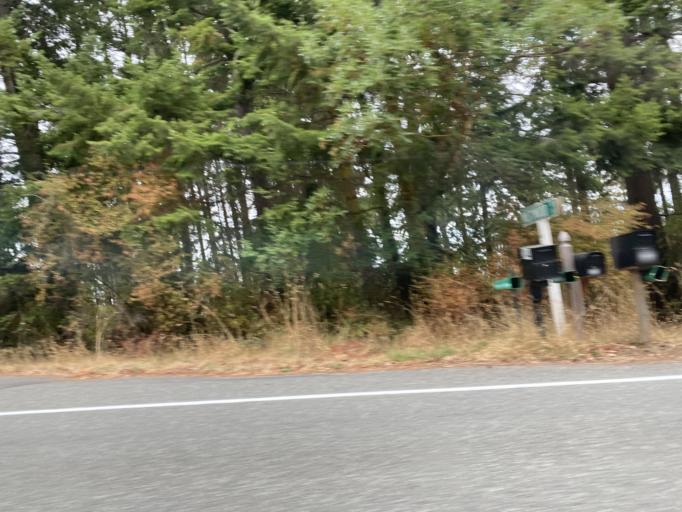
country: US
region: Washington
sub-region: Island County
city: Coupeville
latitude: 48.2206
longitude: -122.6457
